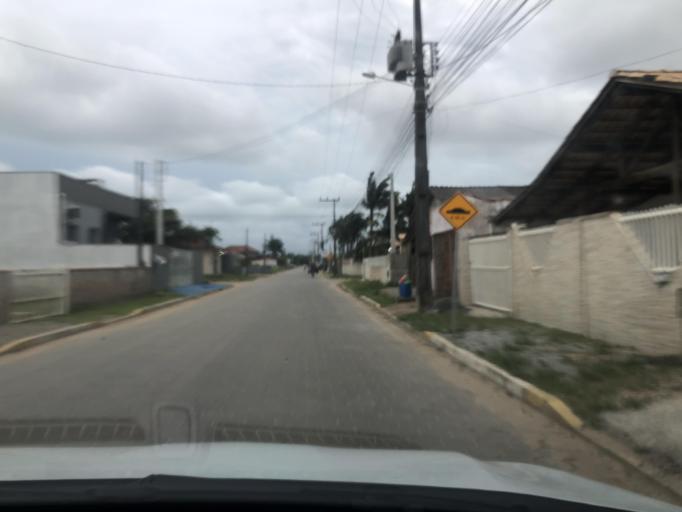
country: BR
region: Santa Catarina
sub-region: Sao Francisco Do Sul
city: Sao Francisco do Sul
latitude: -26.2315
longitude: -48.5243
